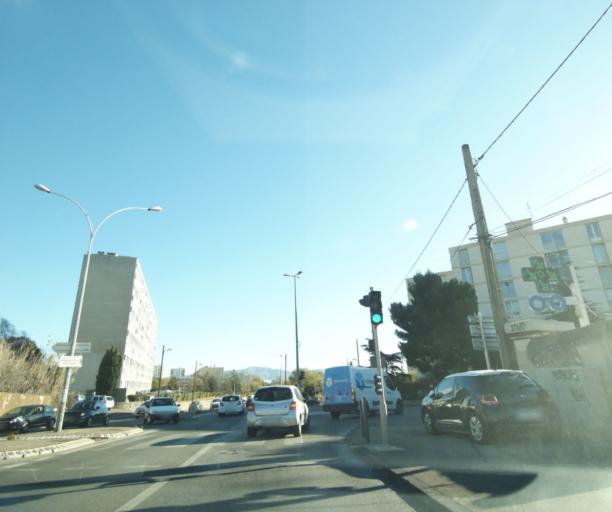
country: FR
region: Provence-Alpes-Cote d'Azur
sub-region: Departement des Bouches-du-Rhone
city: Marseille 14
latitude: 43.3533
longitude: 5.3718
